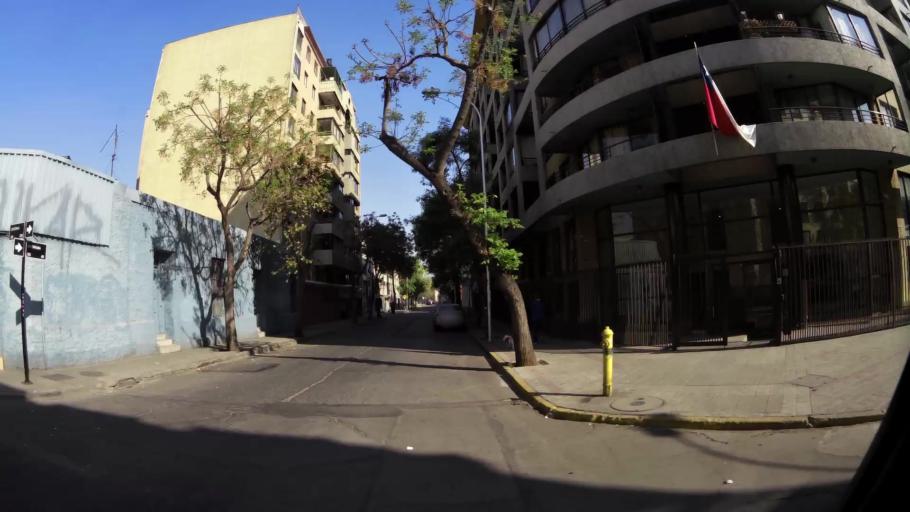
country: CL
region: Santiago Metropolitan
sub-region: Provincia de Santiago
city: Santiago
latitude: -33.4391
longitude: -70.6671
